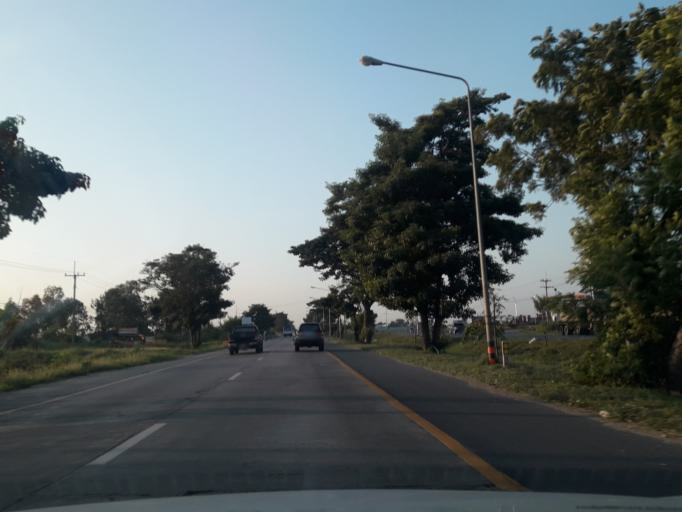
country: TH
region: Phra Nakhon Si Ayutthaya
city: Phra Nakhon Si Ayutthaya
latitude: 14.3327
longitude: 100.5280
